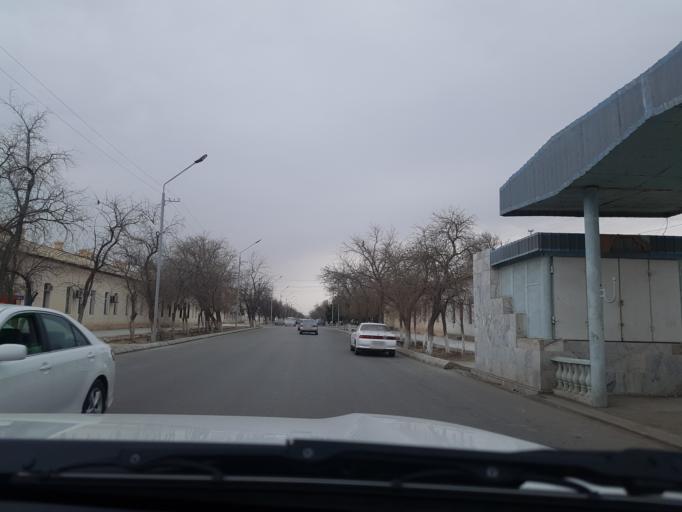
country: TM
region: Balkan
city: Balkanabat
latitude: 39.5057
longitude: 54.3597
